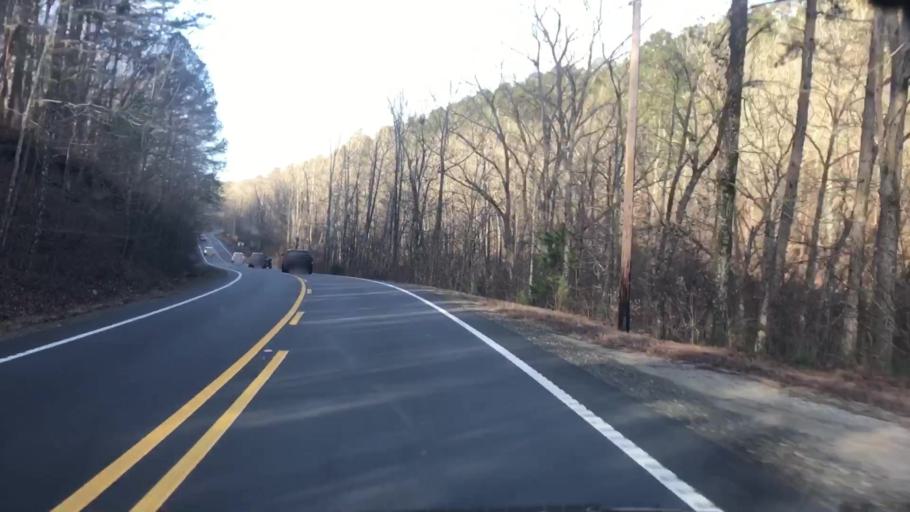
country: US
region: Arkansas
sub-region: Montgomery County
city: Mount Ida
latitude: 34.5245
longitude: -93.4028
